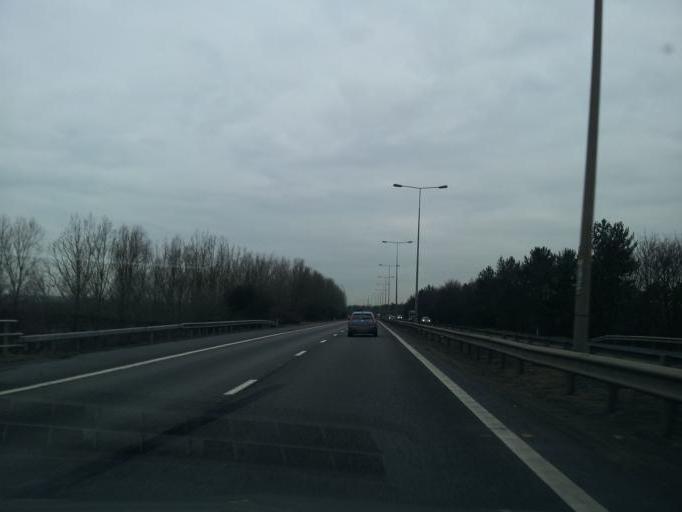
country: GB
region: England
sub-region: Cambridgeshire
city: Girton
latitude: 52.2340
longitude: 0.0672
